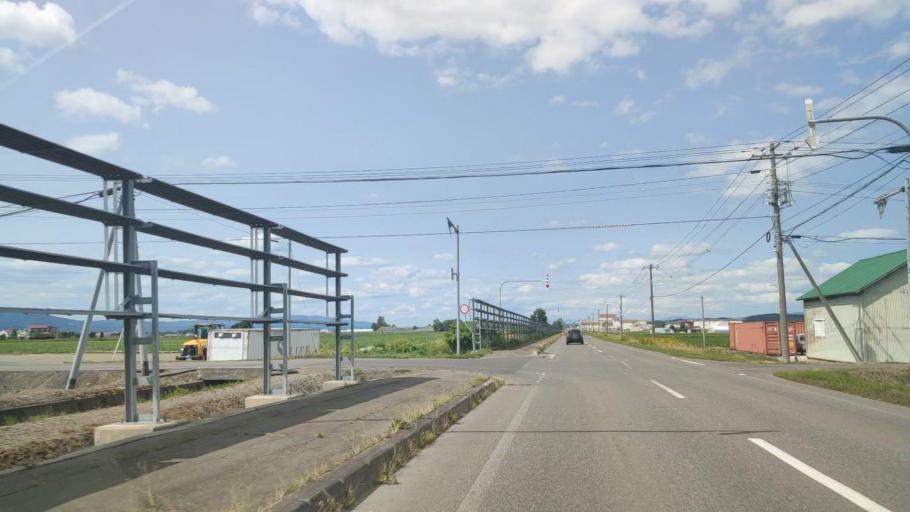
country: JP
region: Hokkaido
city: Nayoro
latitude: 44.1957
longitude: 142.4159
